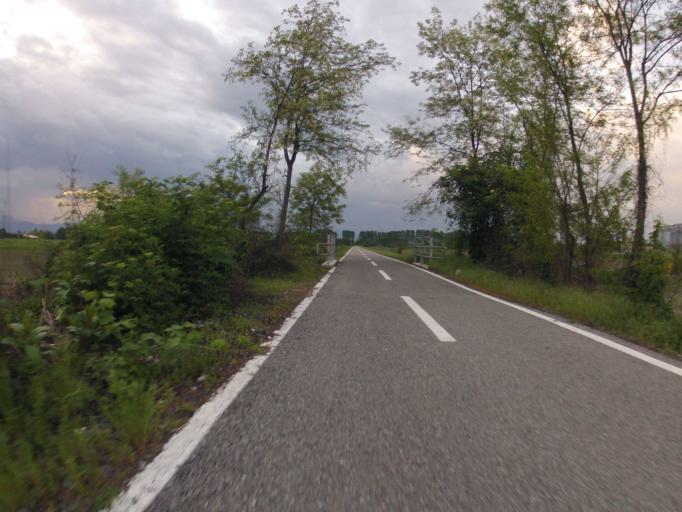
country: IT
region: Piedmont
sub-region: Provincia di Torino
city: Vigone
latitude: 44.8219
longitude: 7.4961
